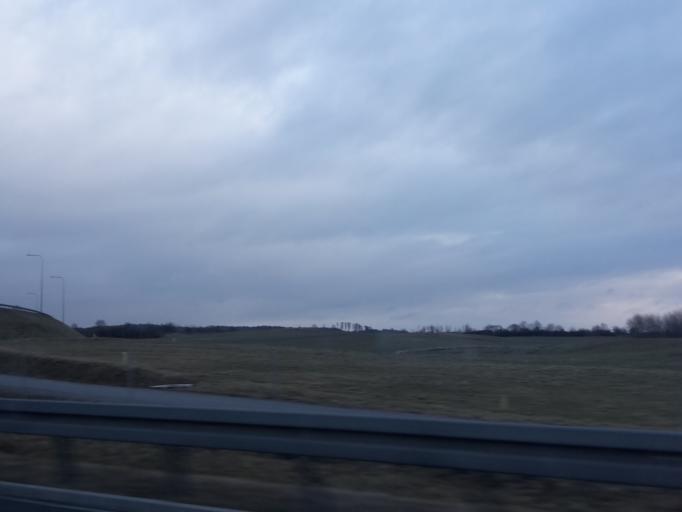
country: PL
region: Warmian-Masurian Voivodeship
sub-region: Powiat ostrodzki
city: Maldyty
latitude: 53.9673
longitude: 19.6979
